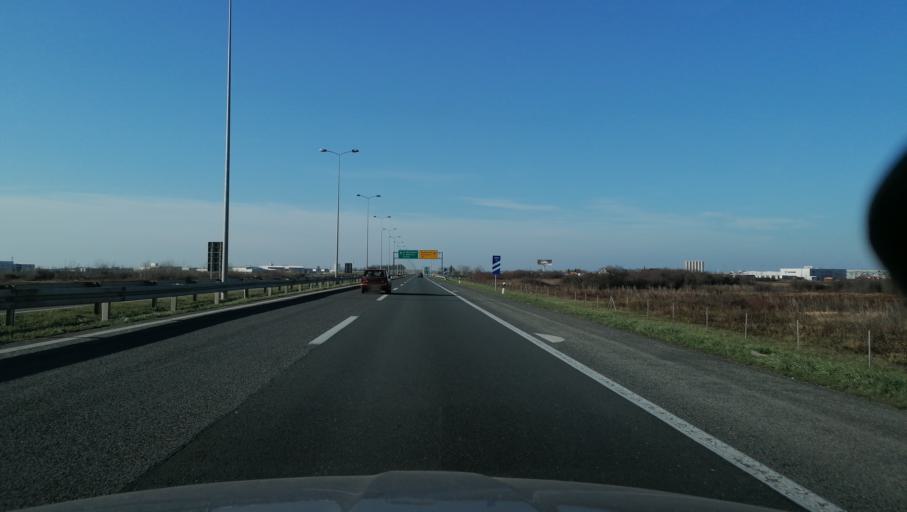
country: RS
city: Simanovci
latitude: 44.8693
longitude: 20.1373
